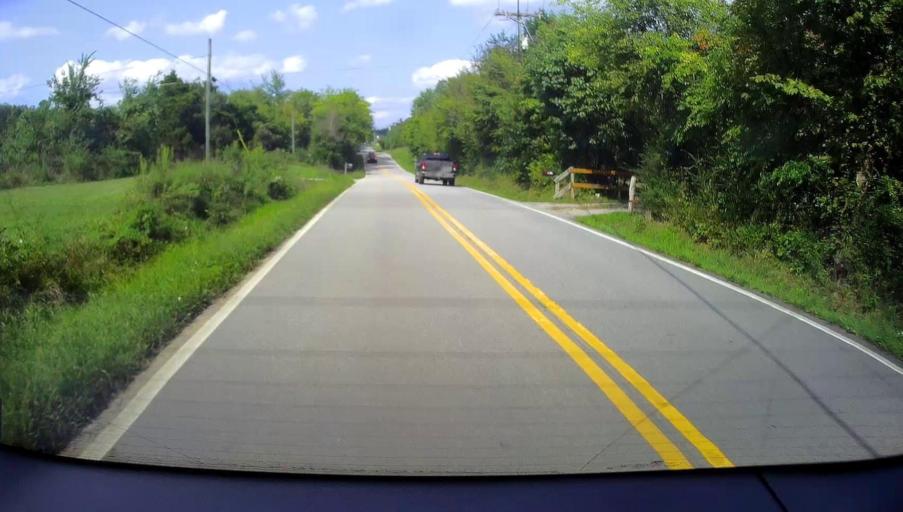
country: US
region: Georgia
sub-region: Catoosa County
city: Ringgold
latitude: 34.9331
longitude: -85.0851
